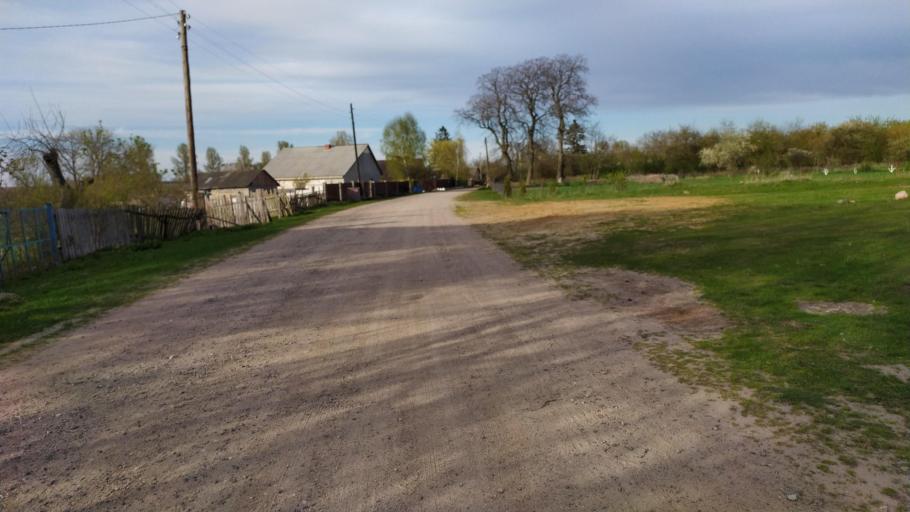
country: BY
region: Brest
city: Kamyanyets
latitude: 52.4073
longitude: 23.6631
